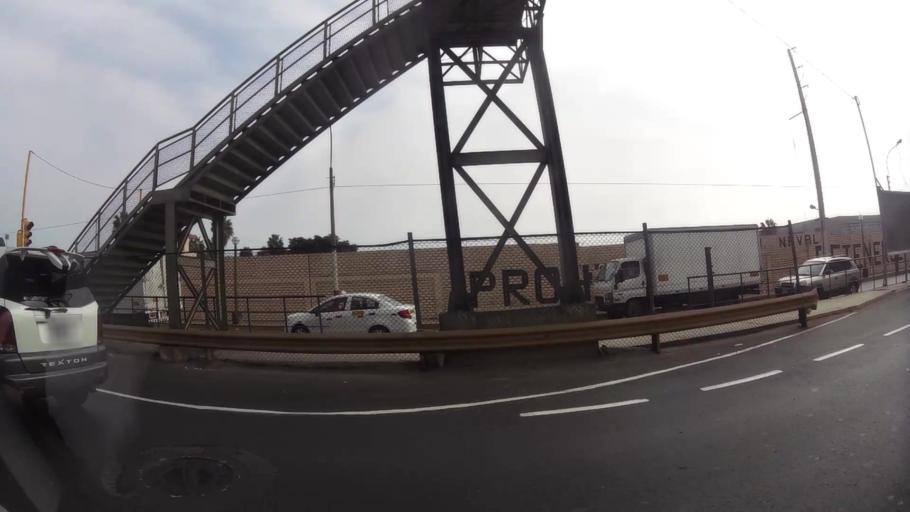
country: PE
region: Callao
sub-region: Callao
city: Callao
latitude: -12.0300
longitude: -77.1021
